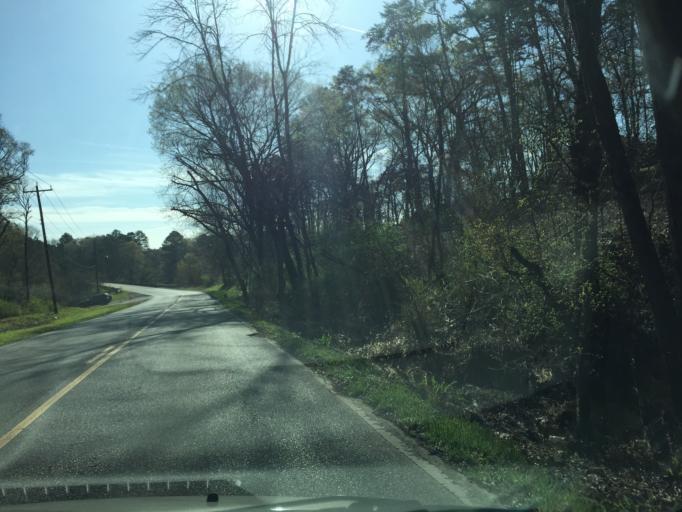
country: US
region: Tennessee
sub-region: Hamilton County
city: East Chattanooga
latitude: 35.0680
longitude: -85.2153
